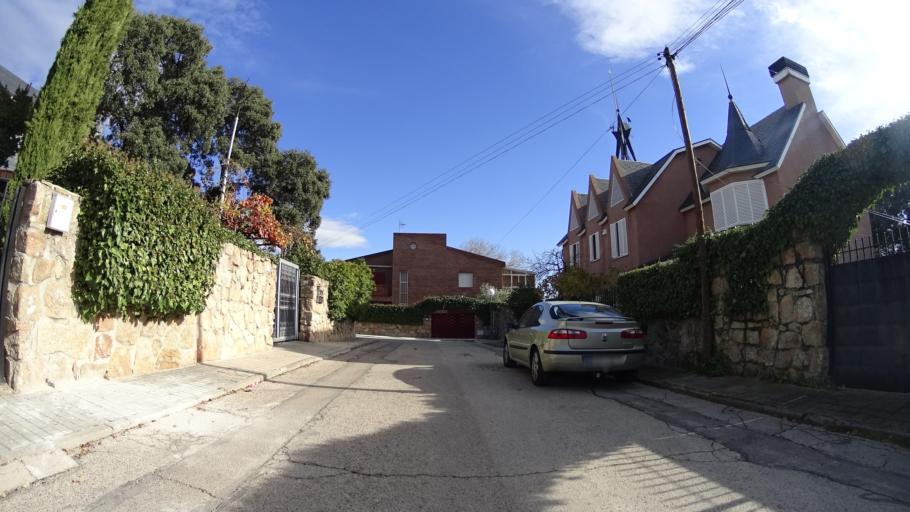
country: ES
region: Madrid
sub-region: Provincia de Madrid
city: Galapagar
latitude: 40.5807
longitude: -4.0175
